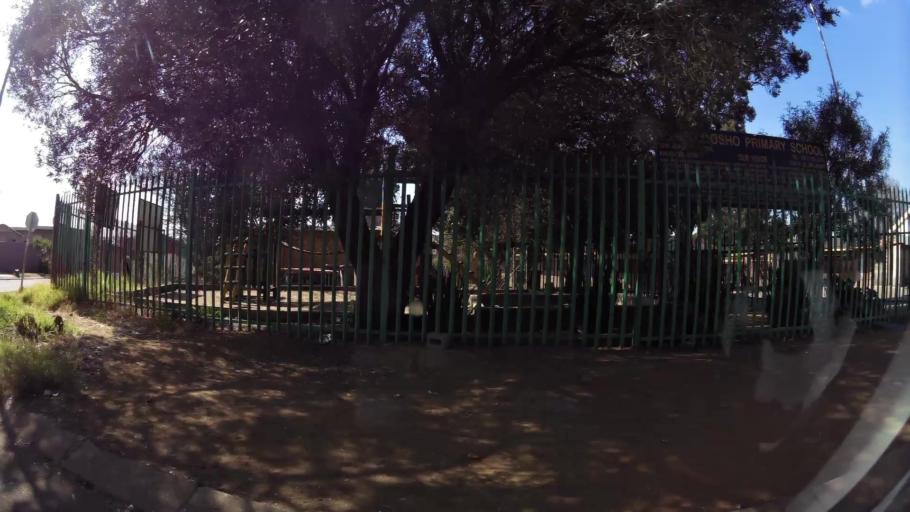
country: ZA
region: Gauteng
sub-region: City of Johannesburg Metropolitan Municipality
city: Soweto
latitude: -26.2495
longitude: 27.8868
